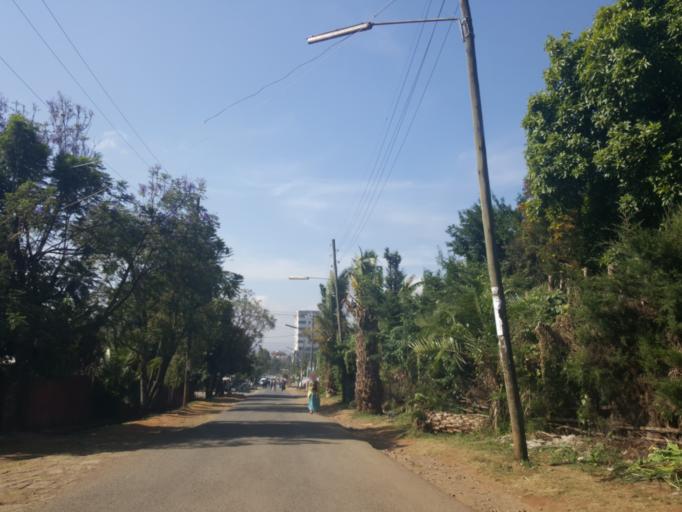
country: ET
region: Adis Abeba
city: Addis Ababa
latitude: 9.0523
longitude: 38.7268
